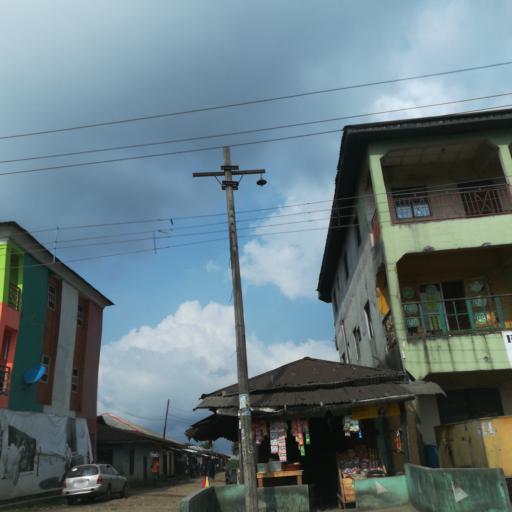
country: NG
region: Rivers
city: Okrika
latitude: 4.7877
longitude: 7.1184
